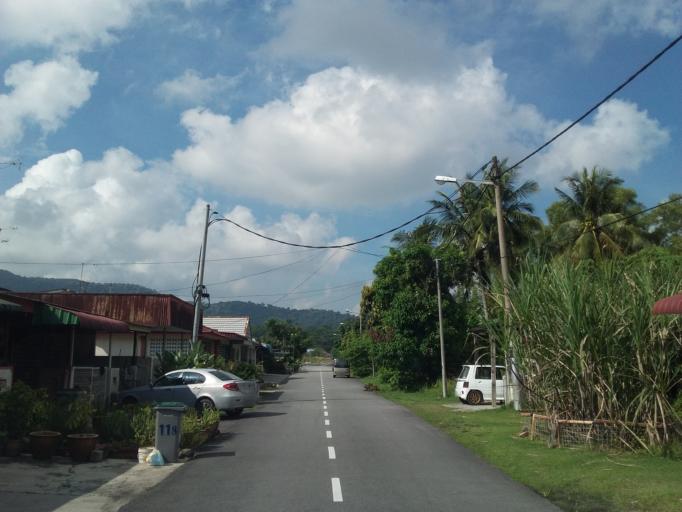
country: MY
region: Johor
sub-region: Daerah Batu Pahat
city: Batu Pahat
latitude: 1.8403
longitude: 102.9252
